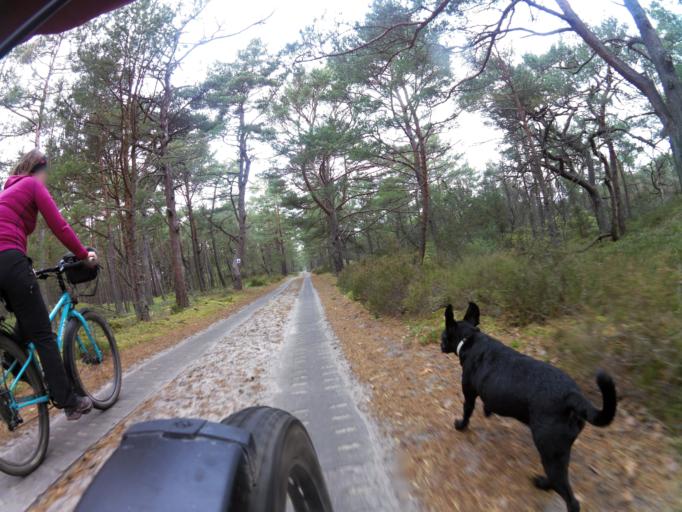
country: PL
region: Pomeranian Voivodeship
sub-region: Powiat pucki
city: Hel
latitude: 54.6243
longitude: 18.8172
